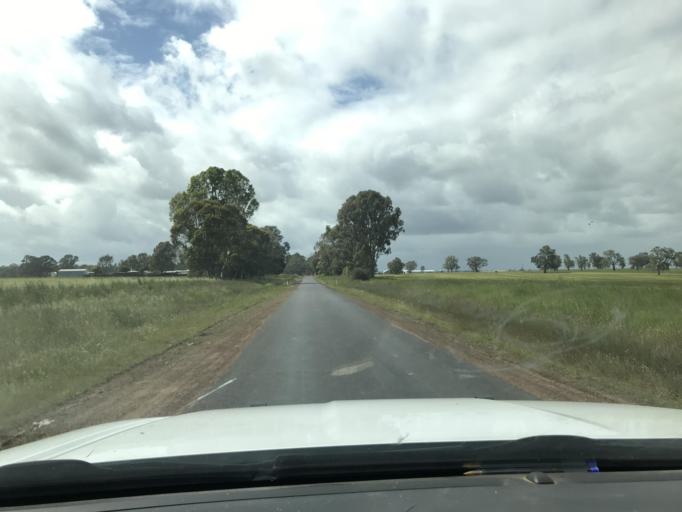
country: AU
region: South Australia
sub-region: Wattle Range
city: Penola
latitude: -37.1484
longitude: 141.3967
